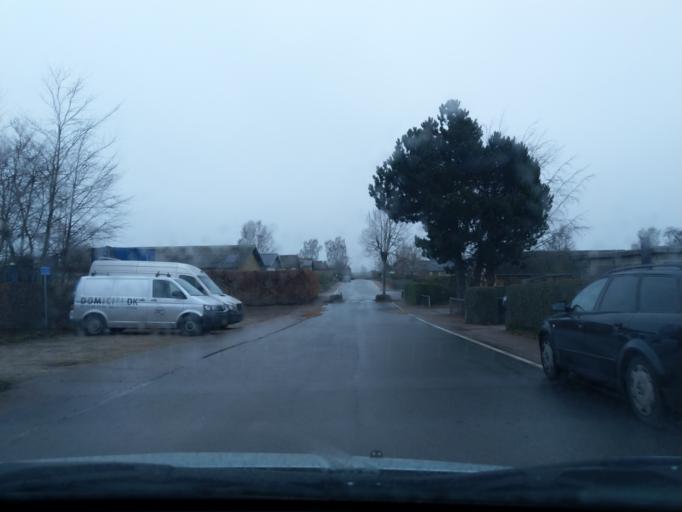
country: DK
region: Zealand
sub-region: Vordingborg Kommune
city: Orslev
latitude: 55.1275
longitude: 11.9487
